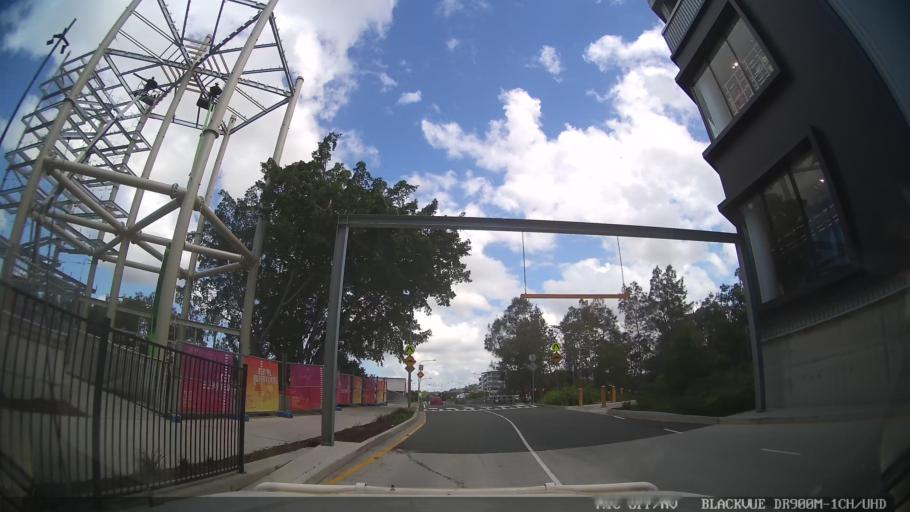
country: AU
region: Queensland
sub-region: Sunshine Coast
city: Buderim
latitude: -26.6552
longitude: 153.0856
